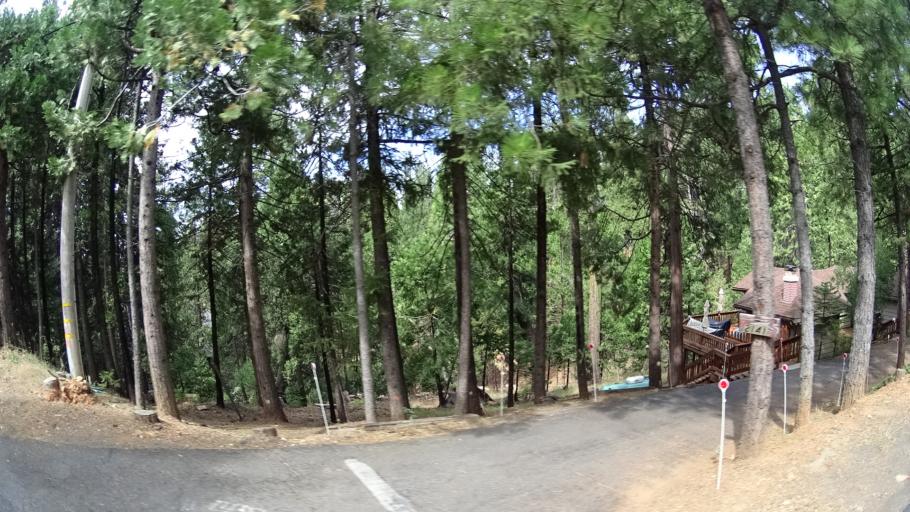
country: US
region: California
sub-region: Calaveras County
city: Arnold
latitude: 38.2455
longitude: -120.3486
